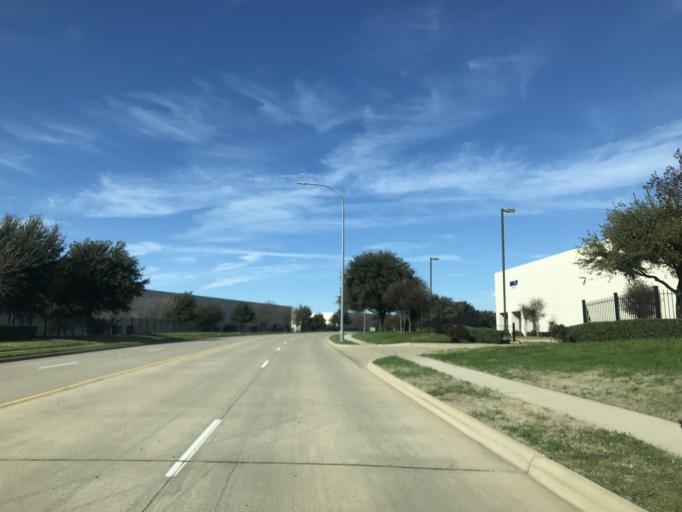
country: US
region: Texas
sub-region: Tarrant County
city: Haltom City
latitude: 32.8311
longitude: -97.3012
